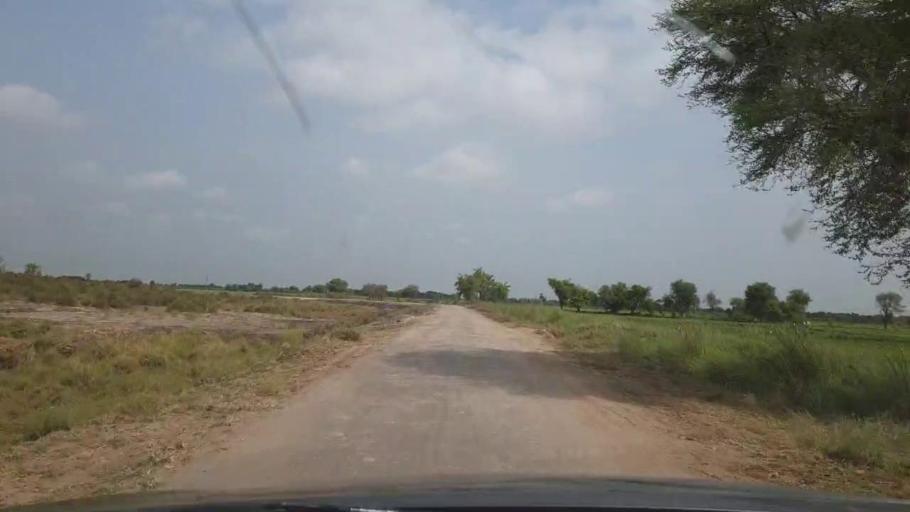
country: PK
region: Sindh
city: Ratodero
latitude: 27.8403
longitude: 68.2979
